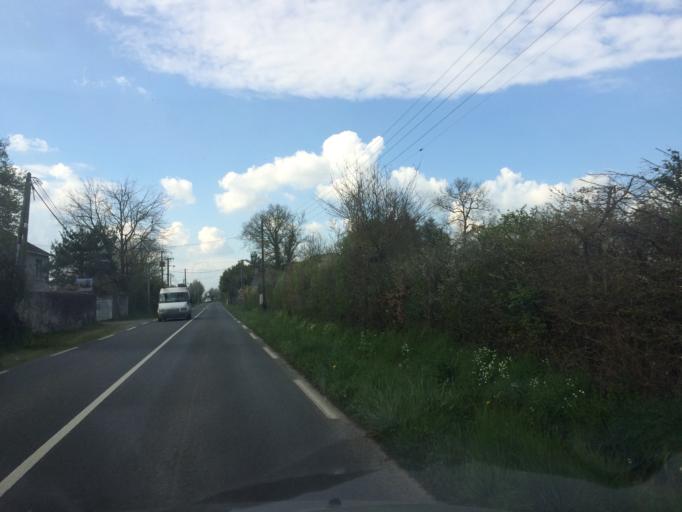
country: FR
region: Pays de la Loire
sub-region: Departement de la Loire-Atlantique
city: Heric
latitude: 47.4208
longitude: -1.6576
